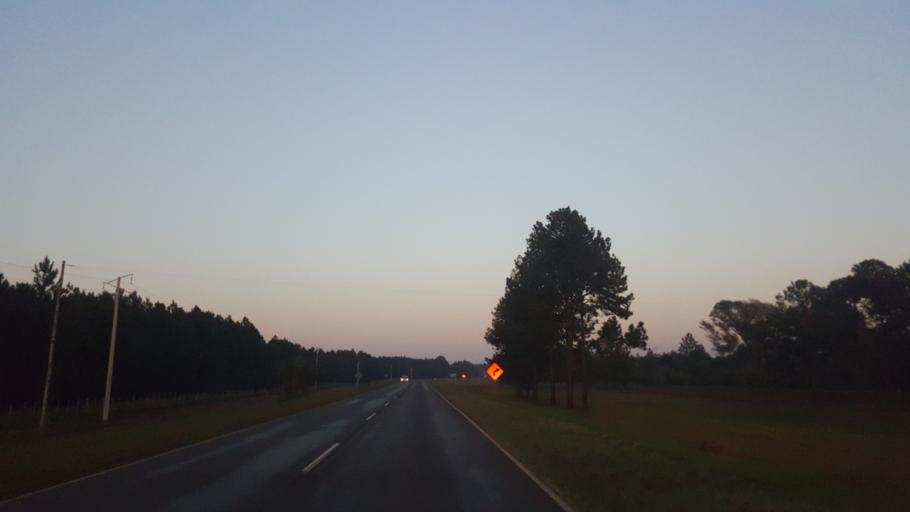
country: AR
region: Corrientes
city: Ituzaingo
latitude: -27.6173
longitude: -56.3870
